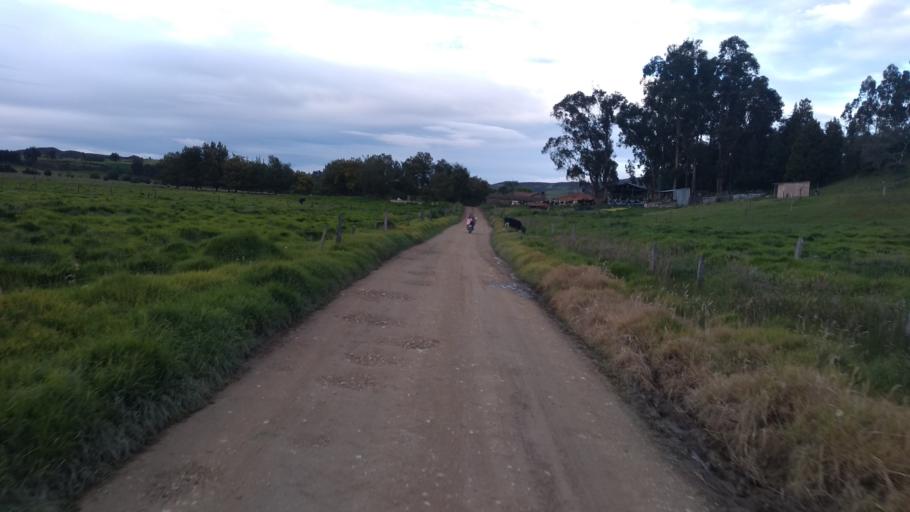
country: CO
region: Boyaca
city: Toca
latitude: 5.6202
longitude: -73.1644
